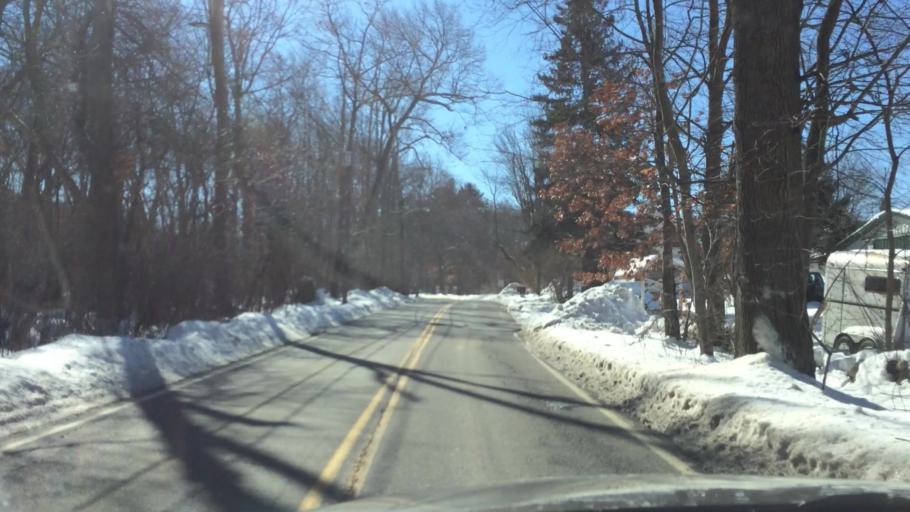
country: US
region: Massachusetts
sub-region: Middlesex County
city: Pinehurst
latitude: 42.5246
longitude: -71.2579
